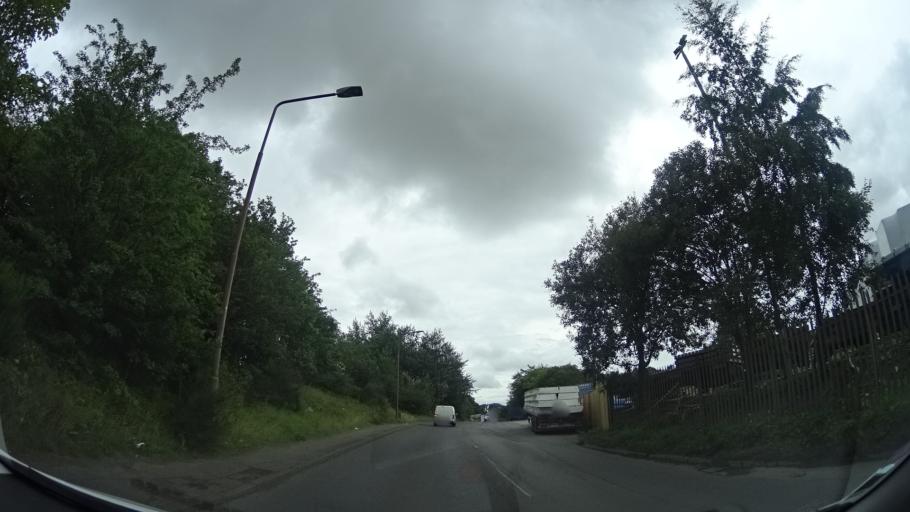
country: GB
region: Scotland
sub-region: Edinburgh
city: Newbridge
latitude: 55.9285
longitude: -3.4147
